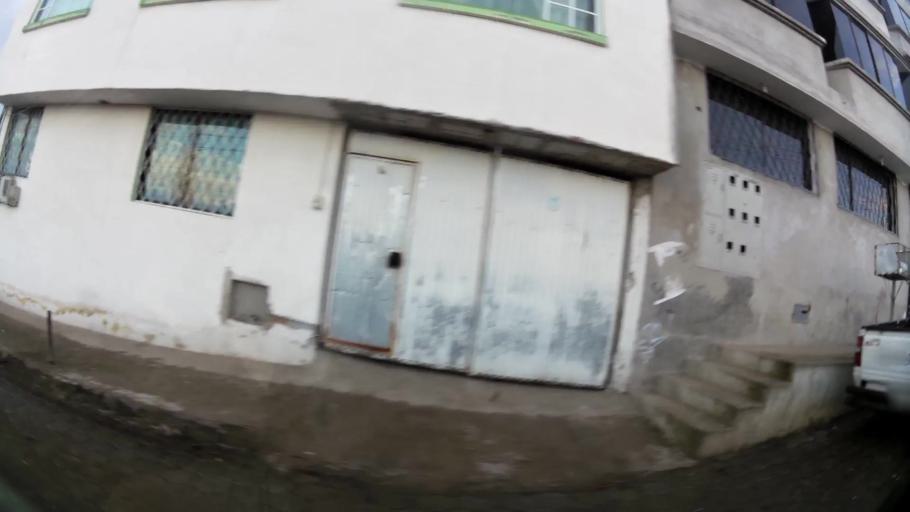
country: EC
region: Pichincha
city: Quito
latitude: -0.0971
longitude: -78.5156
